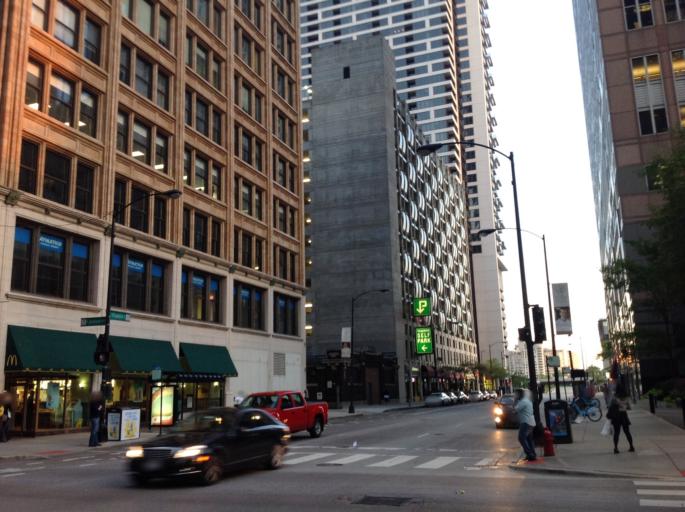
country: US
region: Illinois
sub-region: Cook County
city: Chicago
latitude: 41.8782
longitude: -87.6354
